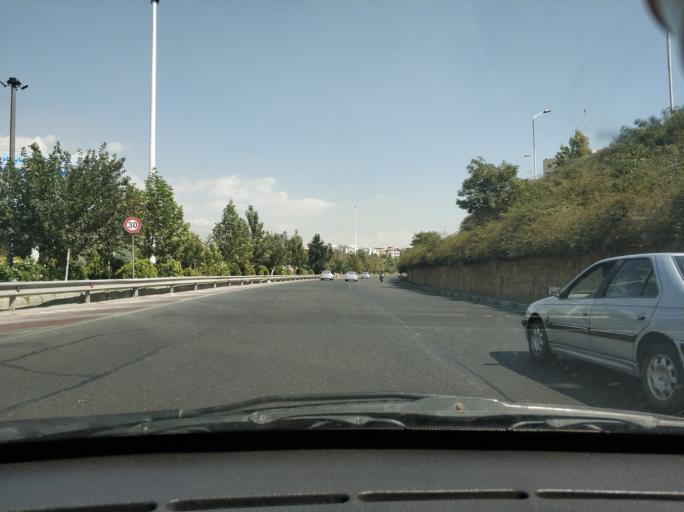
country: IR
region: Tehran
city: Tehran
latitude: 35.7474
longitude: 51.3716
